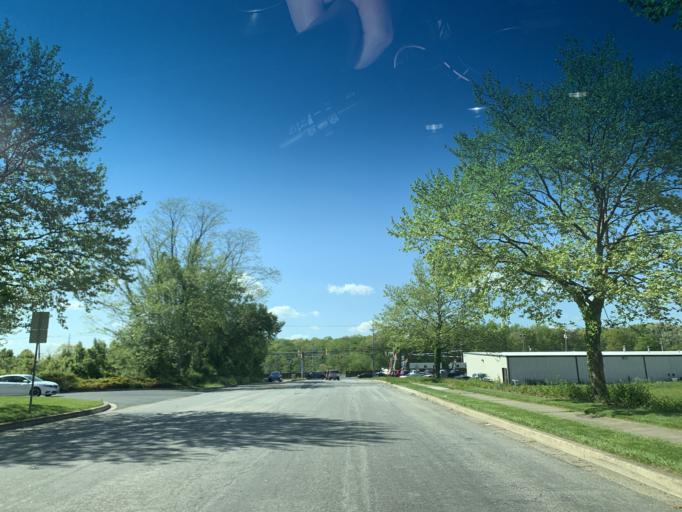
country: US
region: Maryland
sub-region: Harford County
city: Edgewood
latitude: 39.4407
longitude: -76.2915
